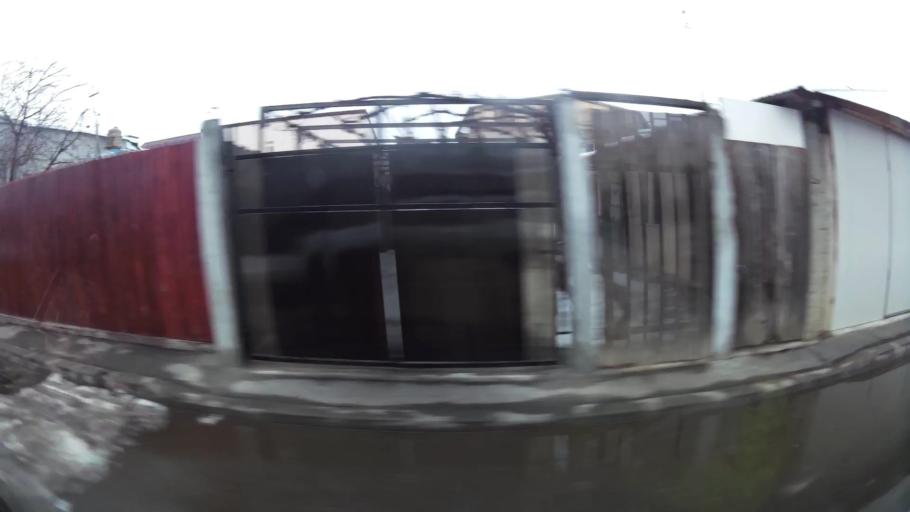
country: RO
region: Ilfov
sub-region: Comuna Magurele
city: Magurele
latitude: 44.3819
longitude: 26.0449
